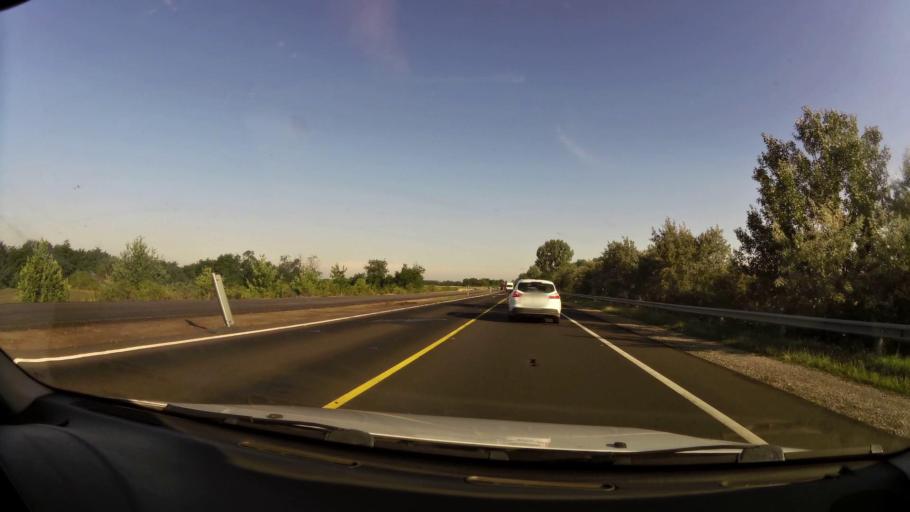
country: HU
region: Pest
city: Cegledbercel
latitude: 47.2419
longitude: 19.6571
